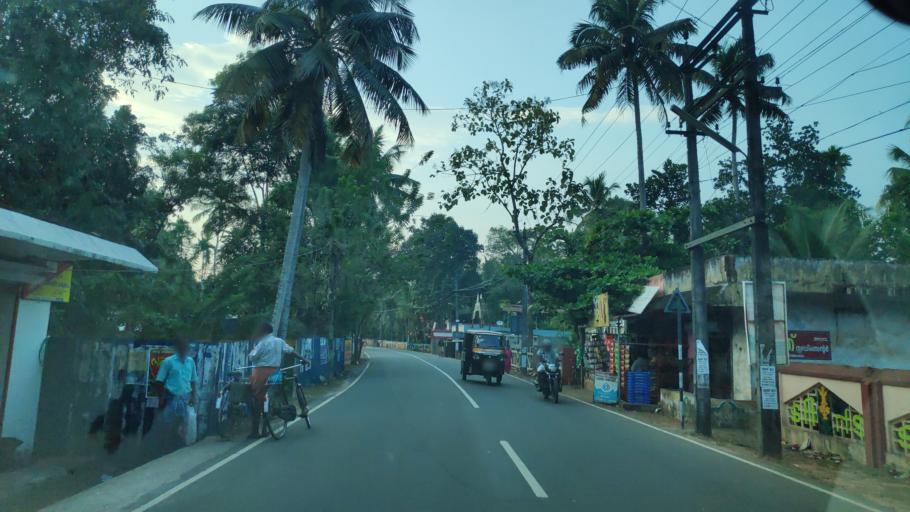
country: IN
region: Kerala
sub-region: Alappuzha
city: Shertallai
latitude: 9.6800
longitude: 76.3736
